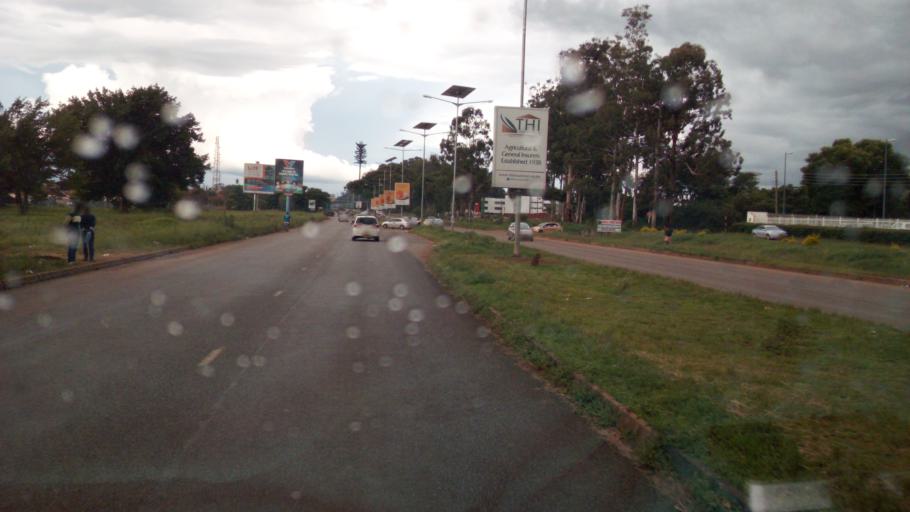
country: ZW
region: Harare
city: Harare
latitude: -17.7850
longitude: 31.0754
